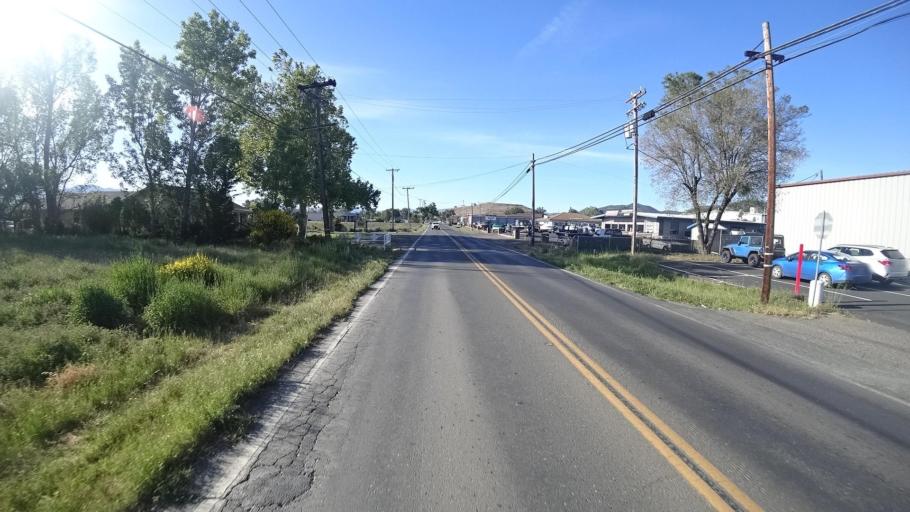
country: US
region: California
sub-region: Lake County
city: Lakeport
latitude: 39.0212
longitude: -122.9139
